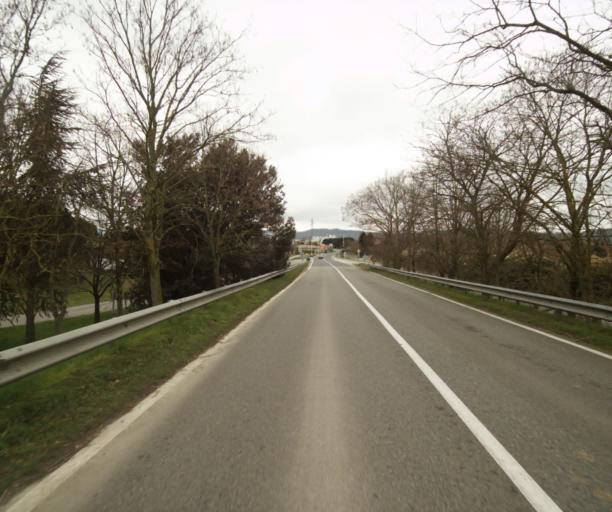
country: FR
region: Midi-Pyrenees
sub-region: Departement de l'Ariege
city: Pamiers
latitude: 43.1340
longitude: 1.6244
